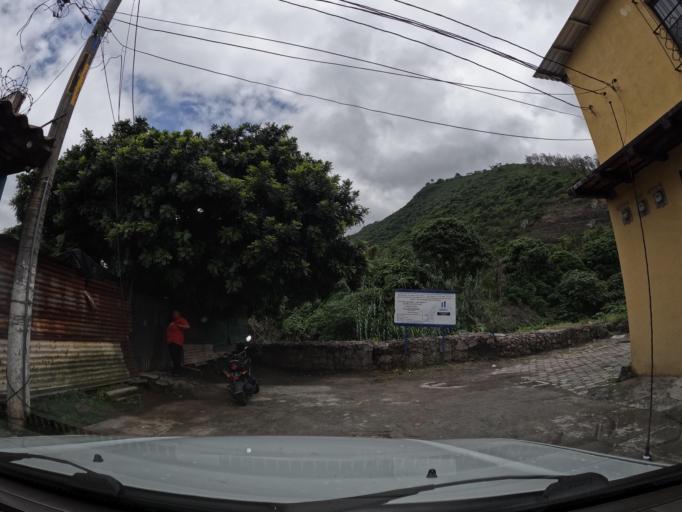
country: GT
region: Sacatepequez
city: Jocotenango
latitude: 14.5782
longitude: -90.7490
